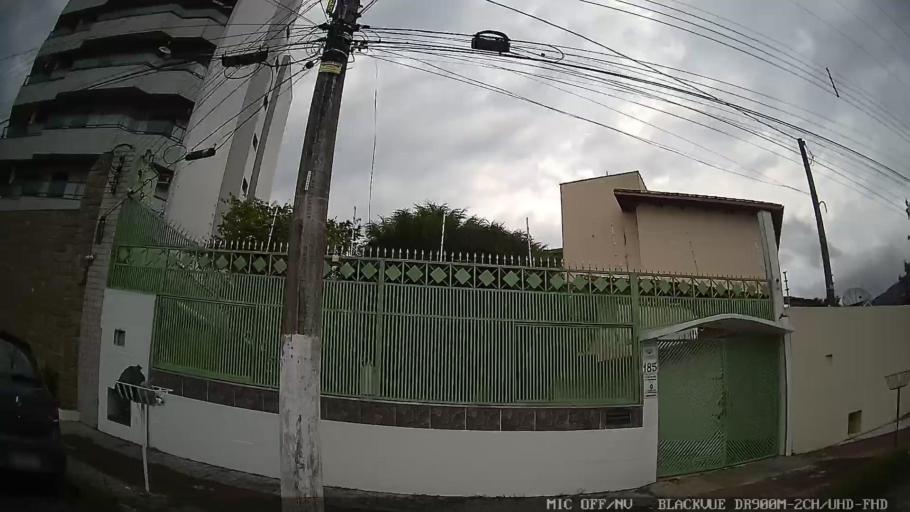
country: BR
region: Sao Paulo
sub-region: Caraguatatuba
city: Caraguatatuba
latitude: -23.6256
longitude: -45.4160
